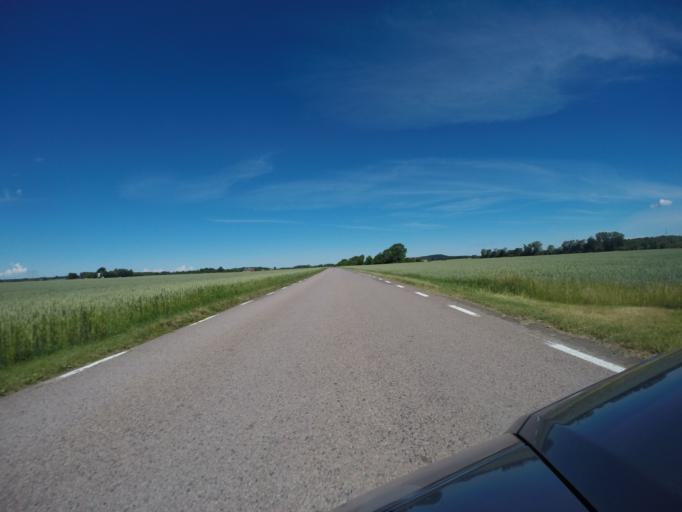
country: SE
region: Skane
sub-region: Helsingborg
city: Odakra
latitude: 56.1378
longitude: 12.7371
